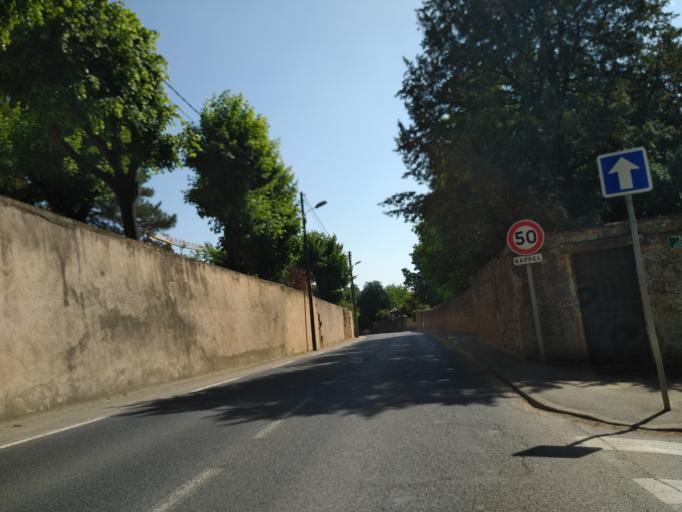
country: FR
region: Rhone-Alpes
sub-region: Departement du Rhone
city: Caluire-et-Cuire
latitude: 45.8064
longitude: 4.8208
